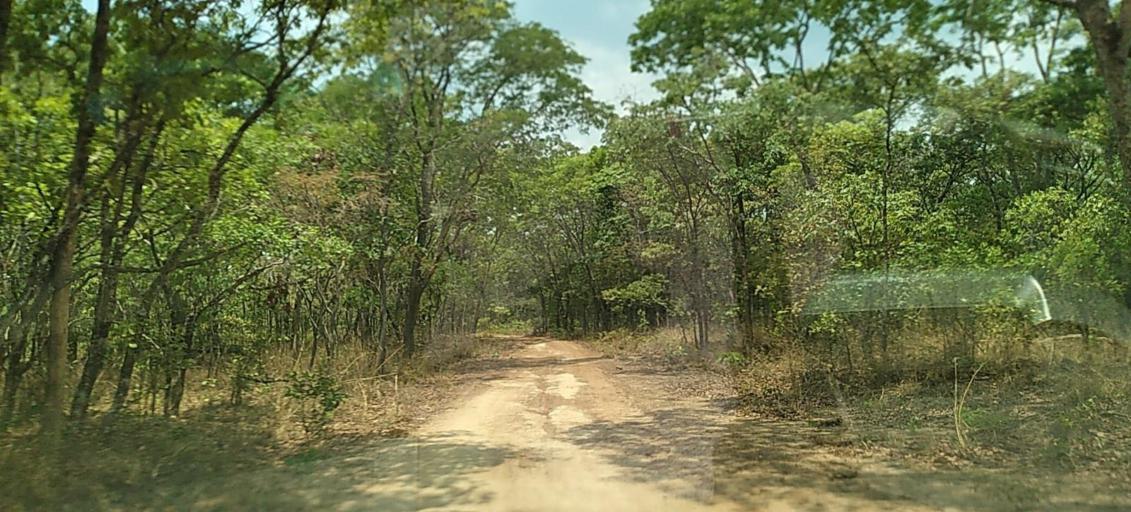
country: ZM
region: Copperbelt
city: Chingola
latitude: -12.7720
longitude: 27.6803
